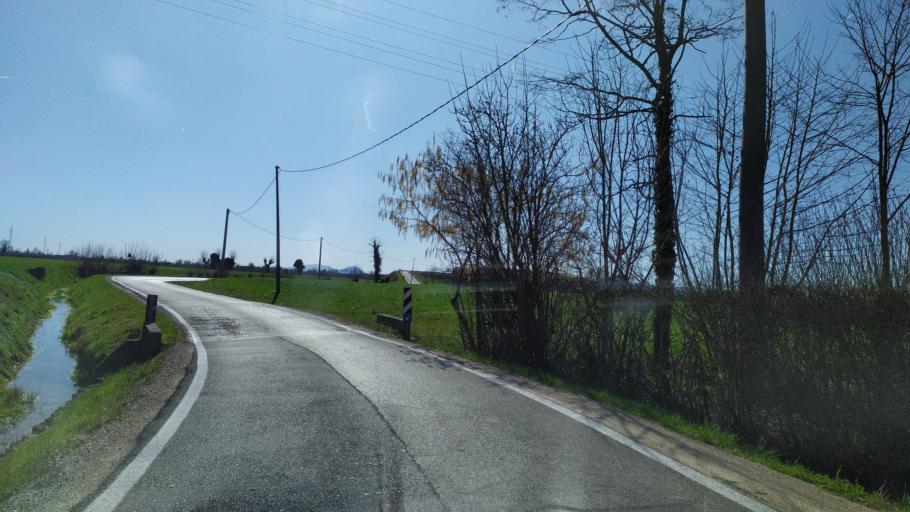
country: IT
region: Veneto
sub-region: Provincia di Vicenza
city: Vigardolo
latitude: 45.6228
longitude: 11.5986
